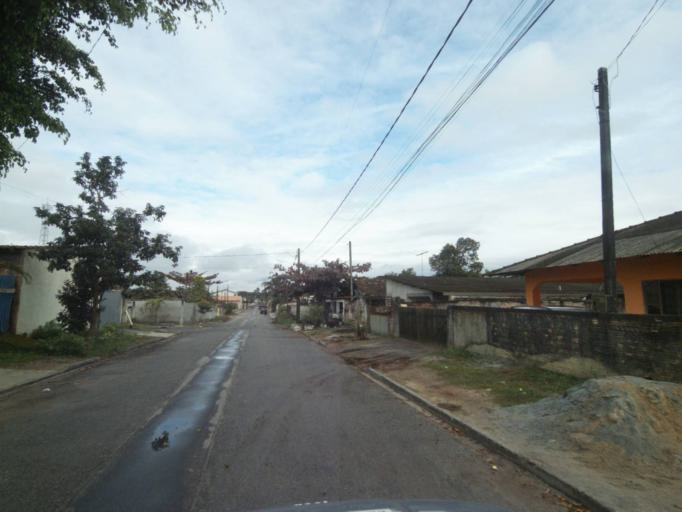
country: BR
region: Parana
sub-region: Paranagua
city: Paranagua
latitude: -25.5619
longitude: -48.5687
